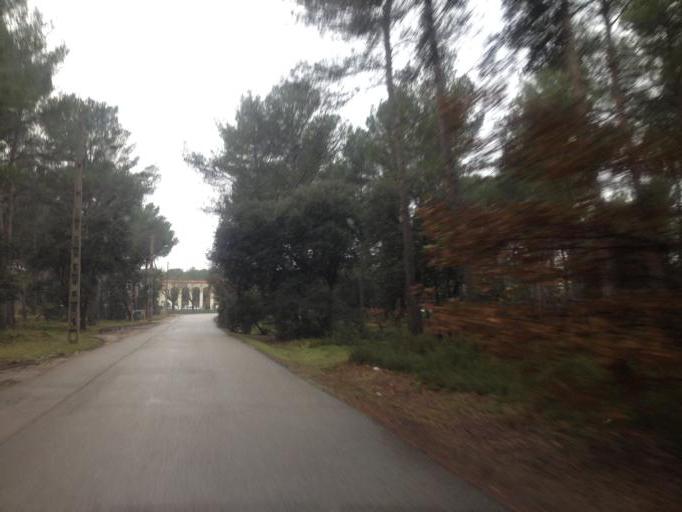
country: FR
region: Provence-Alpes-Cote d'Azur
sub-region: Departement des Bouches-du-Rhone
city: Ventabren
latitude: 43.4900
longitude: 5.3343
